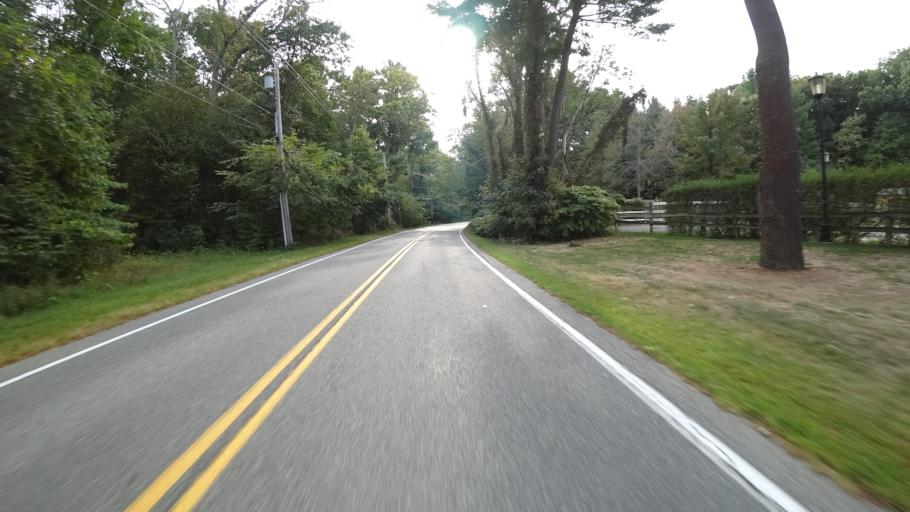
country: US
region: Massachusetts
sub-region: Norfolk County
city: Needham
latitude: 42.2569
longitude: -71.2328
